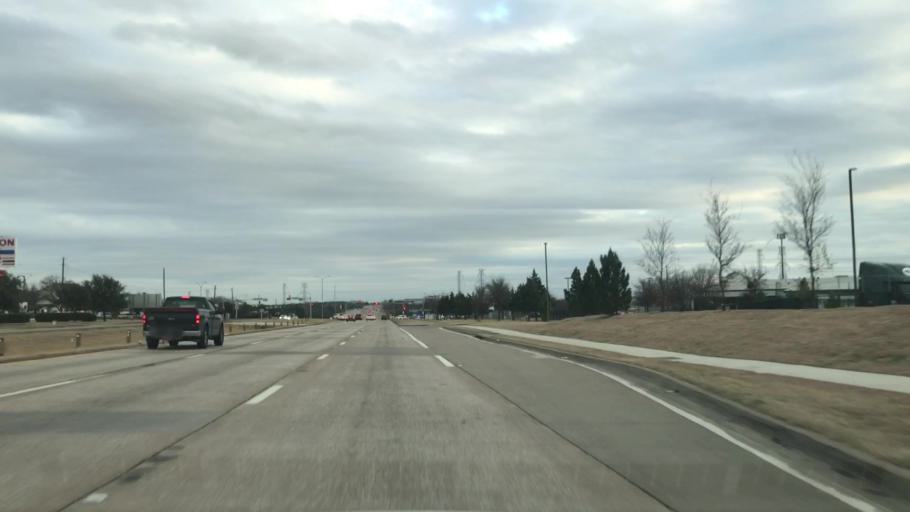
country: US
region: Texas
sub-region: Dallas County
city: Cockrell Hill
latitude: 32.7131
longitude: -96.9105
